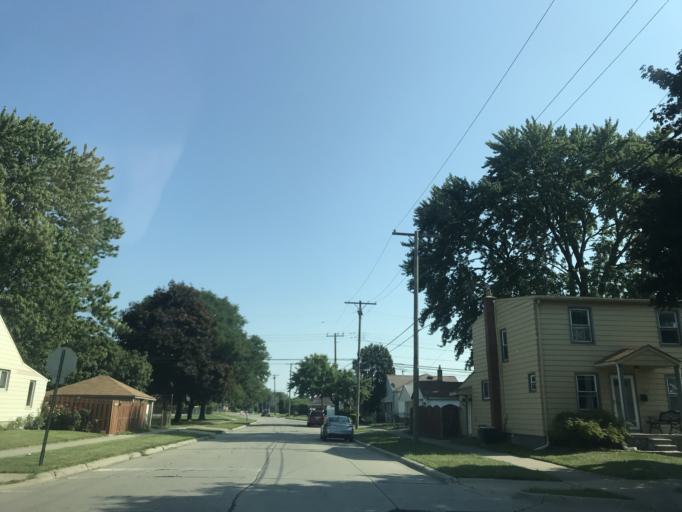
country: US
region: Michigan
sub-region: Wayne County
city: Allen Park
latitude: 42.2677
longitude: -83.1941
